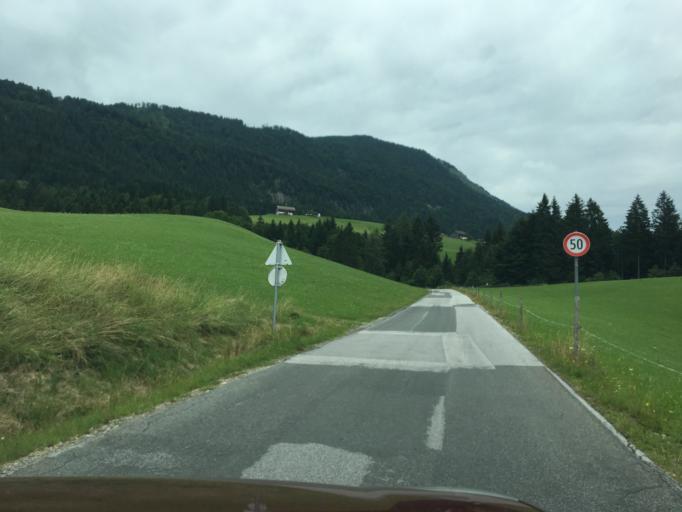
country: AT
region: Salzburg
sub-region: Politischer Bezirk Hallein
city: Abtenau
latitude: 47.5972
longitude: 13.3328
